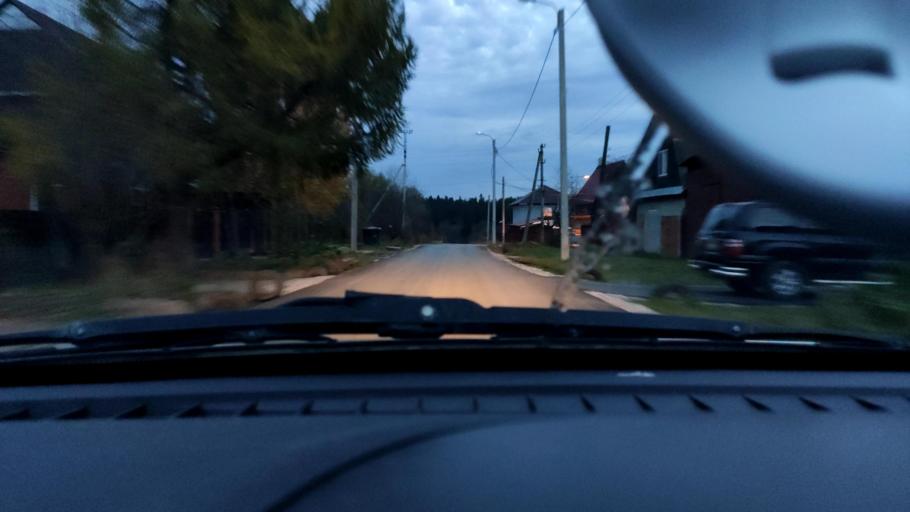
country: RU
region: Perm
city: Perm
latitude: 57.9761
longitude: 56.2988
